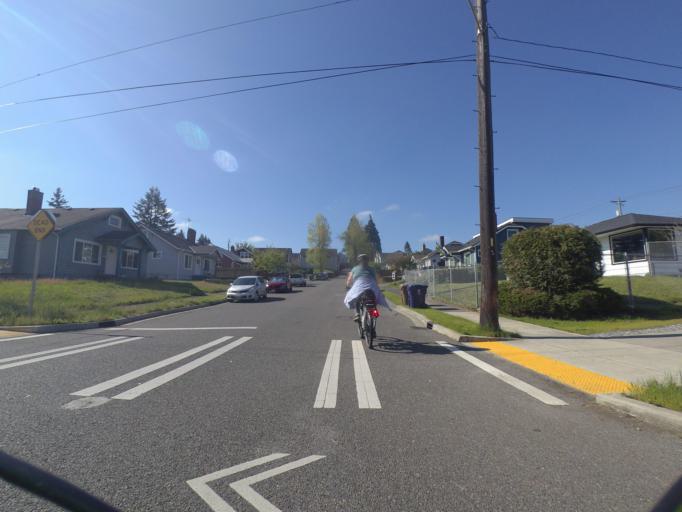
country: US
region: Washington
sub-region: Pierce County
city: Tacoma
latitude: 47.2211
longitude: -122.4188
